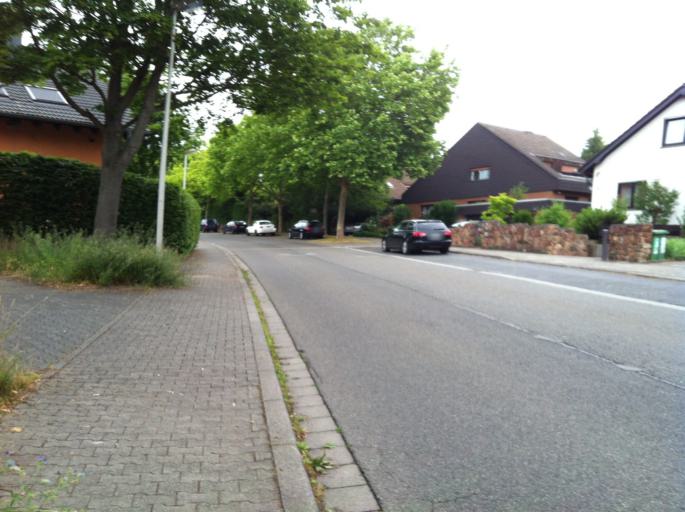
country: DE
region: Rheinland-Pfalz
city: Ober-Olm
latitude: 49.9751
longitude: 8.1965
